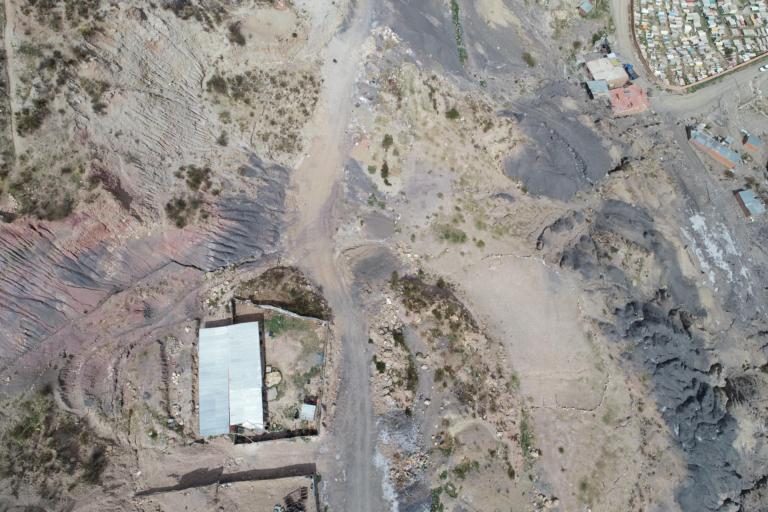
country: BO
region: La Paz
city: La Paz
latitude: -16.5530
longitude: -68.0537
